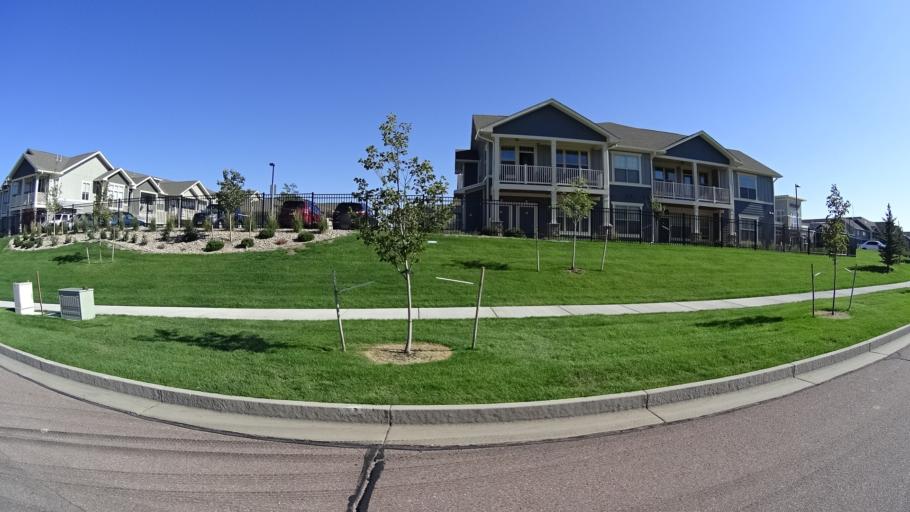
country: US
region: Colorado
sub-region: El Paso County
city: Gleneagle
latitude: 38.9943
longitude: -104.8006
